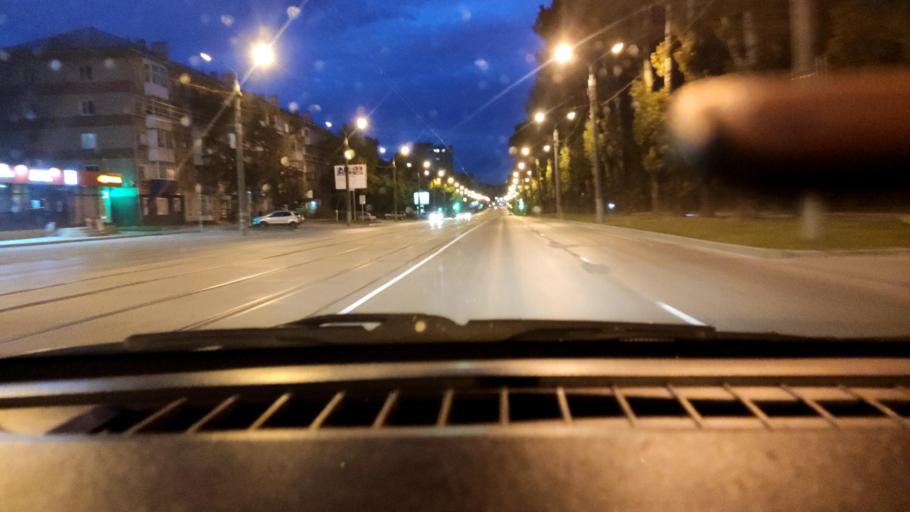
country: RU
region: Perm
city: Perm
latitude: 57.9817
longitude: 56.2013
